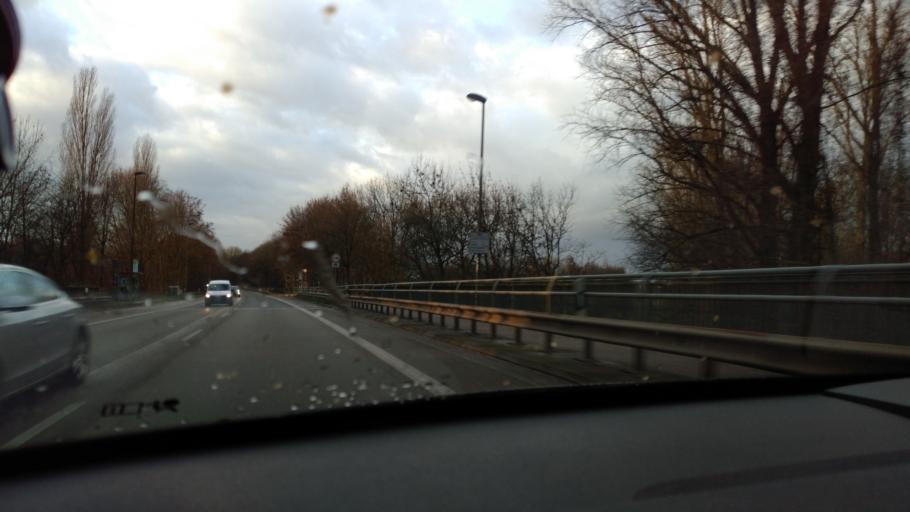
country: DE
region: North Rhine-Westphalia
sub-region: Regierungsbezirk Koln
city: Bonn
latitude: 50.7670
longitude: 7.1049
